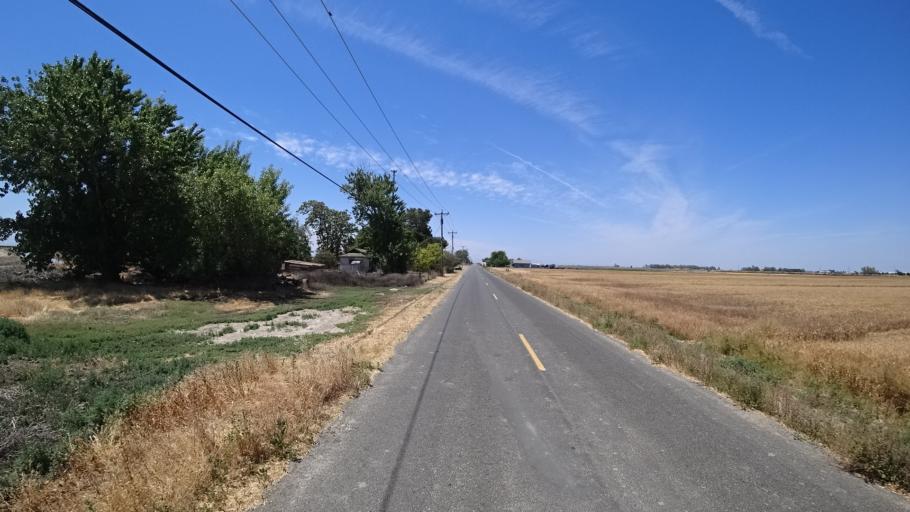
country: US
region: California
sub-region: Kings County
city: Stratford
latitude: 36.2330
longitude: -119.7851
